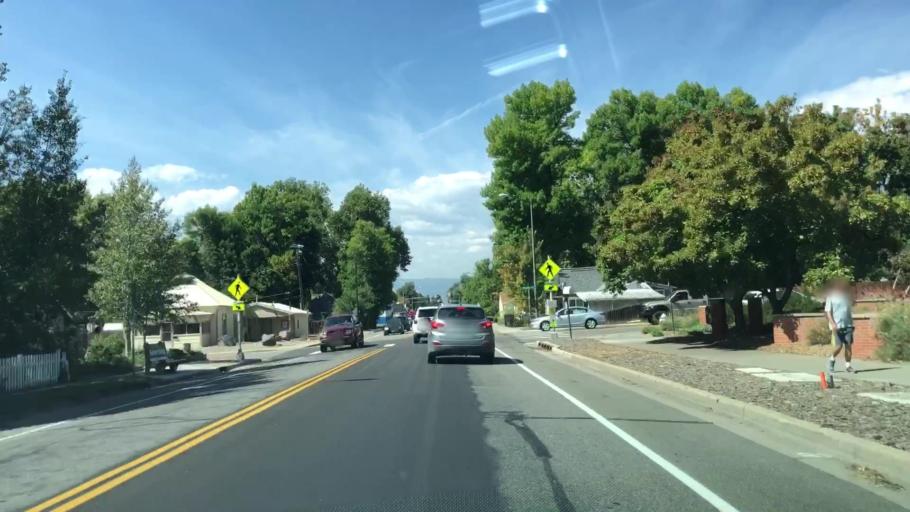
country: US
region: Colorado
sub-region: Larimer County
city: Loveland
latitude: 40.3928
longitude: -105.0702
